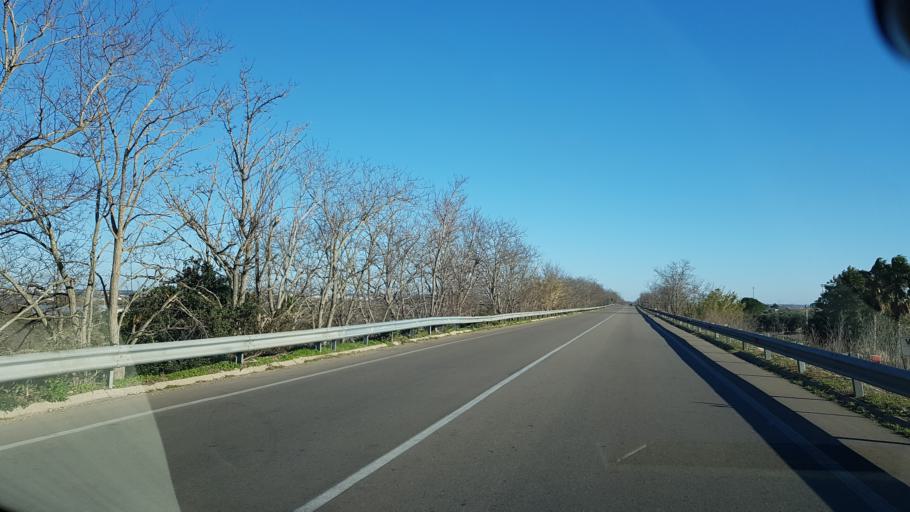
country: IT
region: Apulia
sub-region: Provincia di Lecce
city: Taviano
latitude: 39.9975
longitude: 18.0815
